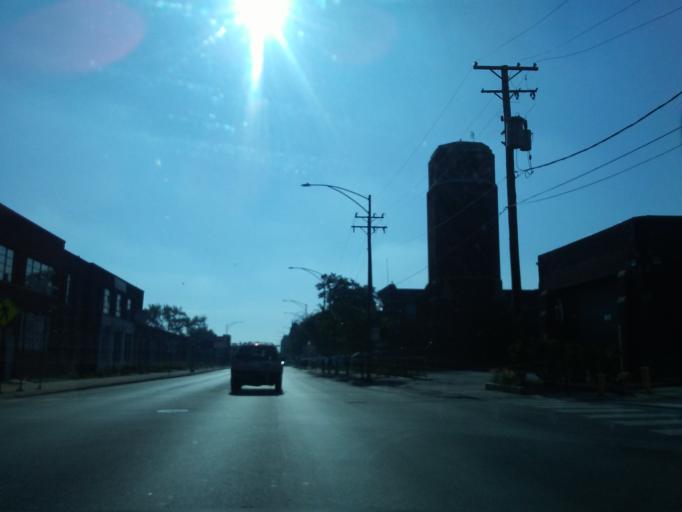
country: US
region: Illinois
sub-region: Cook County
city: Lincolnwood
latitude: 41.9390
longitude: -87.7340
